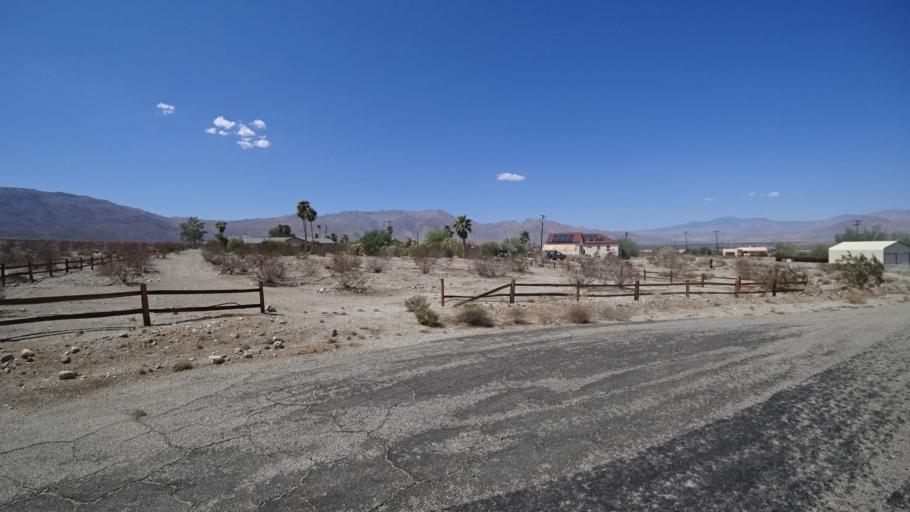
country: US
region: California
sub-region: San Diego County
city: Borrego Springs
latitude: 33.2064
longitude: -116.3401
